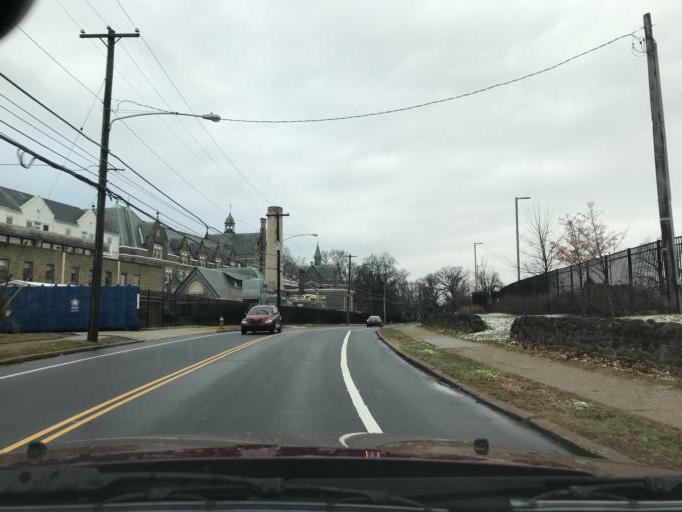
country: US
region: Pennsylvania
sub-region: Montgomery County
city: Bala-Cynwyd
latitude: 39.9971
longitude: -75.2168
